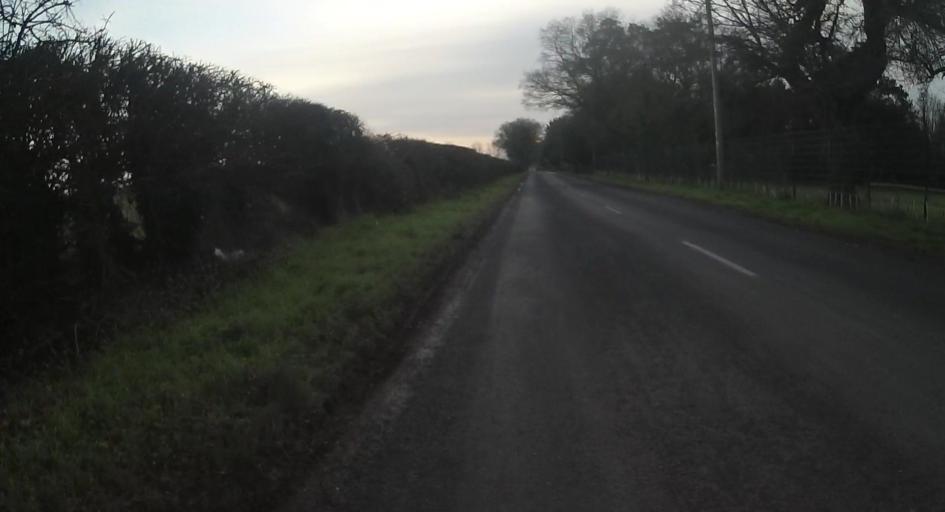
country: GB
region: England
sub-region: Hampshire
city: Overton
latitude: 51.2508
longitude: -1.3317
